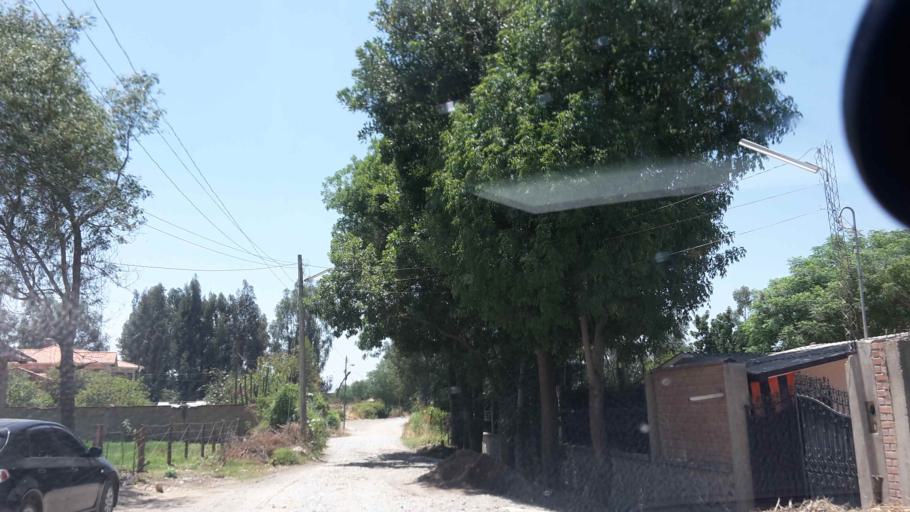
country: BO
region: Cochabamba
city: Cochabamba
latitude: -17.3576
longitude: -66.2043
